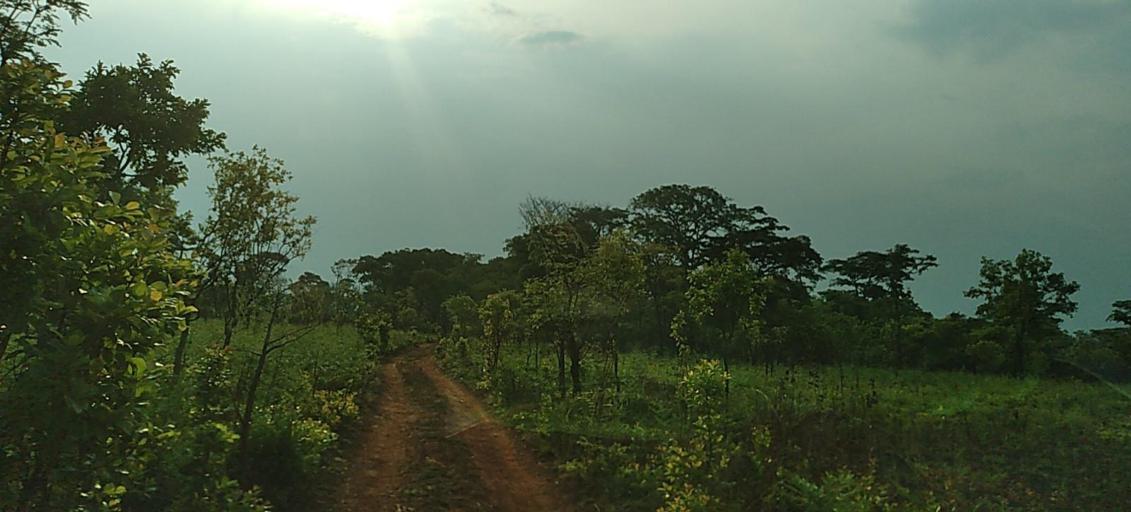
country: ZM
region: North-Western
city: Solwezi
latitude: -12.0429
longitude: 26.0489
